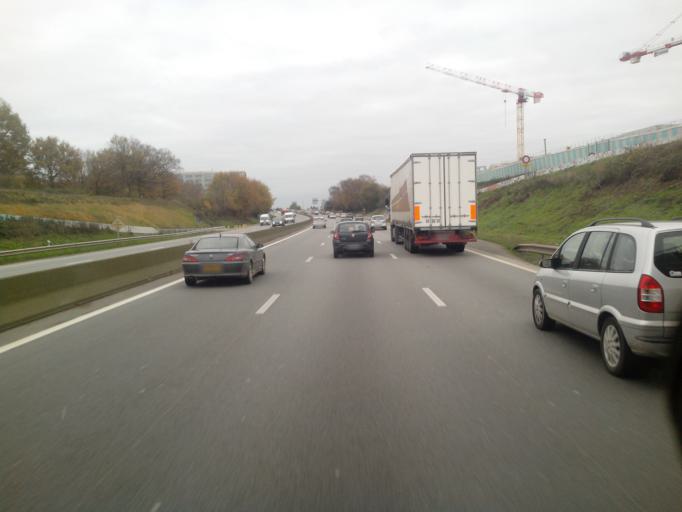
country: FR
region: Brittany
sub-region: Departement d'Ille-et-Vilaine
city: Saint-Jacques-de-la-Lande
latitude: 48.0960
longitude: -1.7119
